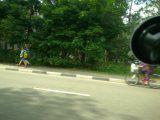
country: RU
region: Moskovskaya
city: Zhukovskiy
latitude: 55.5983
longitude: 38.1345
